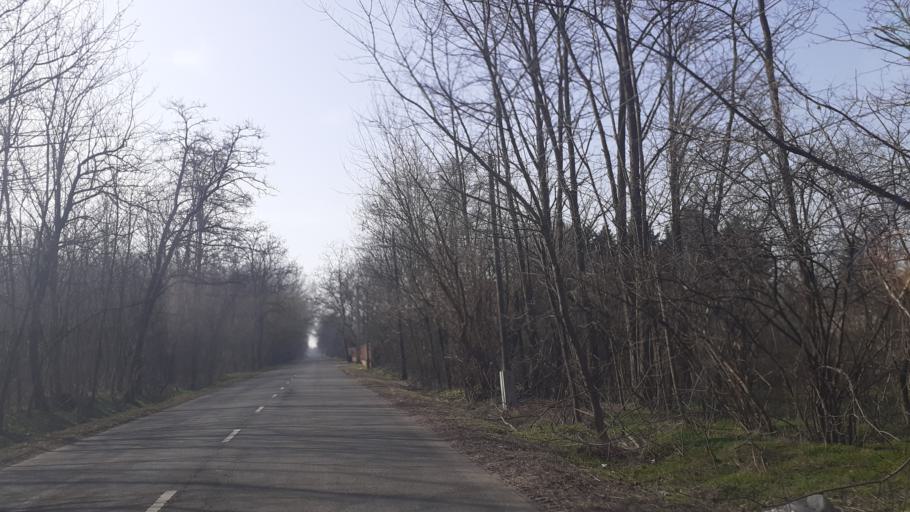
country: HU
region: Pest
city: Orkeny
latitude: 47.1196
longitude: 19.4149
